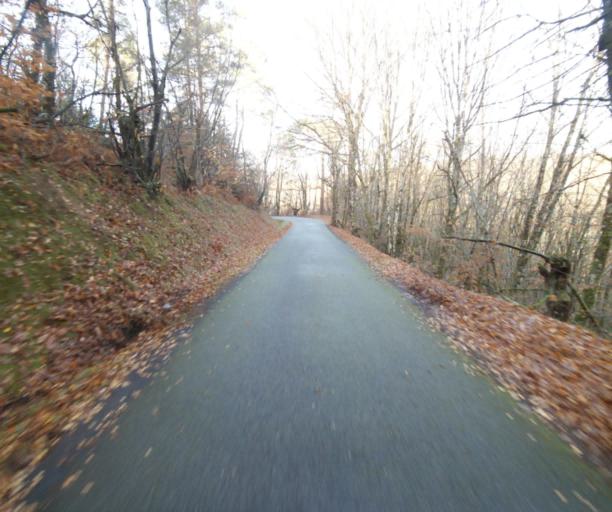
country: FR
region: Limousin
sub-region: Departement de la Correze
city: Laguenne
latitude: 45.2635
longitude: 1.8004
